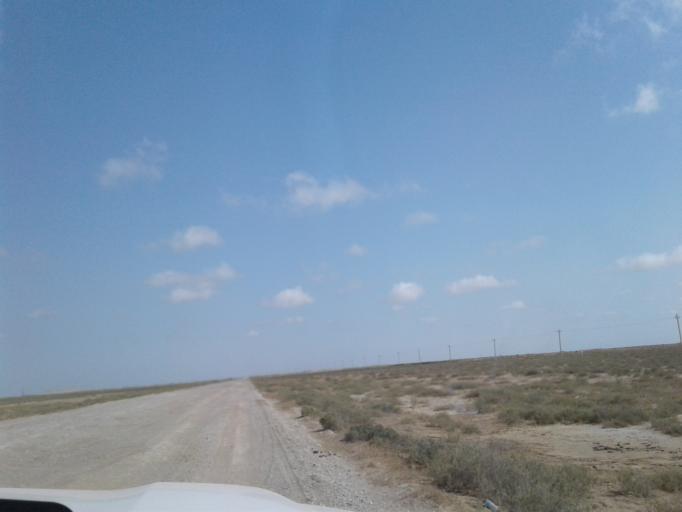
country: IR
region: Golestan
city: Gomishan
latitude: 37.6724
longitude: 53.9352
